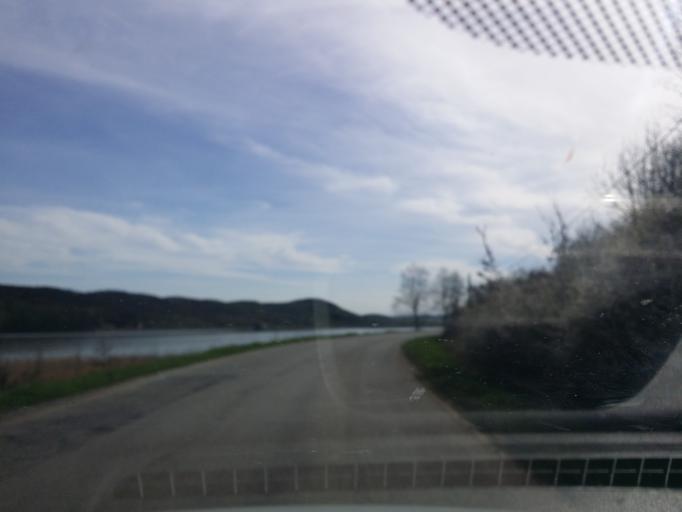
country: HU
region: Borsod-Abauj-Zemplen
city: Szendro
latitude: 48.4544
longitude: 20.7699
